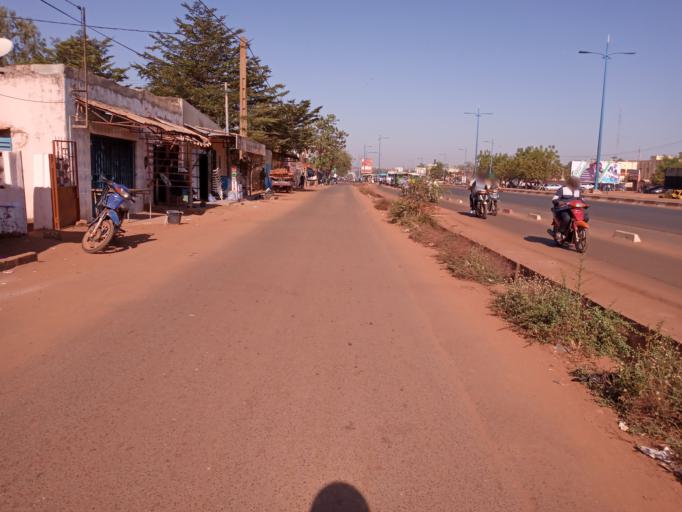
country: ML
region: Bamako
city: Bamako
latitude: 12.5999
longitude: -7.9637
